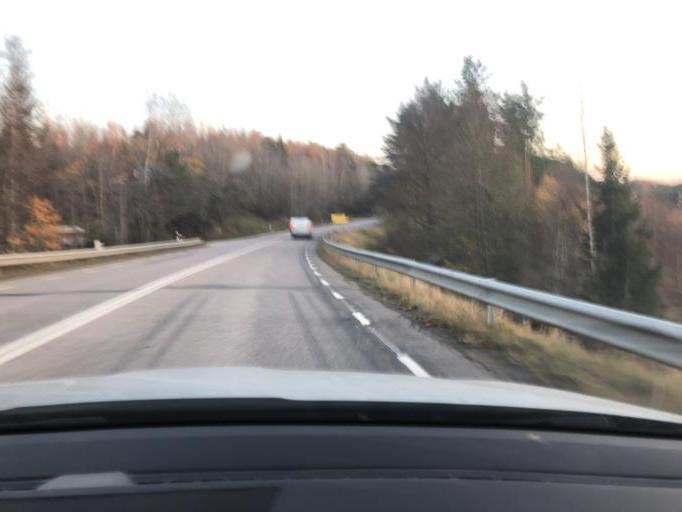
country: SE
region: Soedermanland
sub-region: Strangnas Kommun
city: Akers Styckebruk
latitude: 59.3079
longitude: 17.0909
